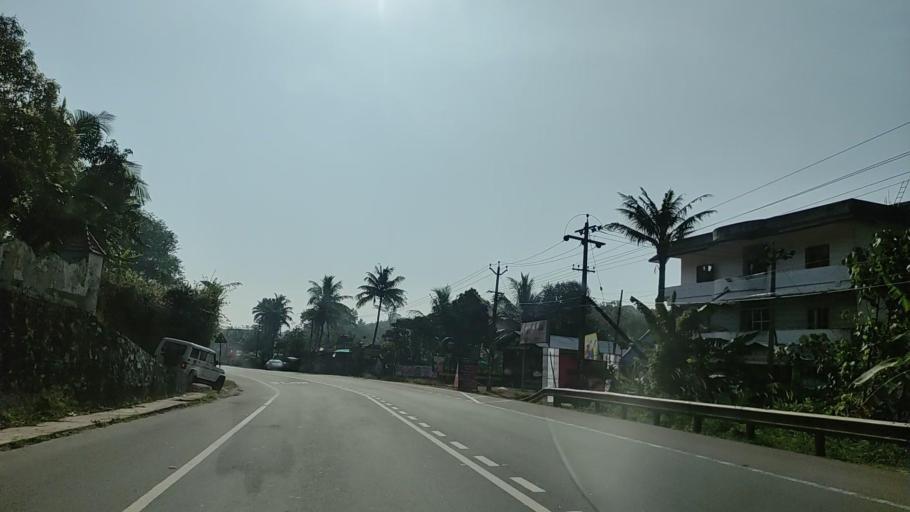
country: IN
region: Kerala
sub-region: Kollam
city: Punalur
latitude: 8.9603
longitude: 76.8386
